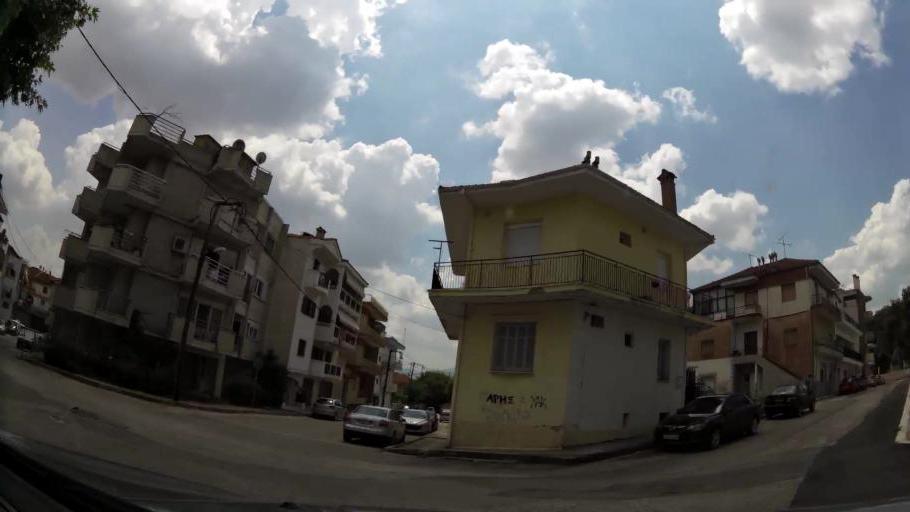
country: GR
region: West Macedonia
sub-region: Nomos Kozanis
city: Kozani
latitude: 40.2957
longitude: 21.7841
